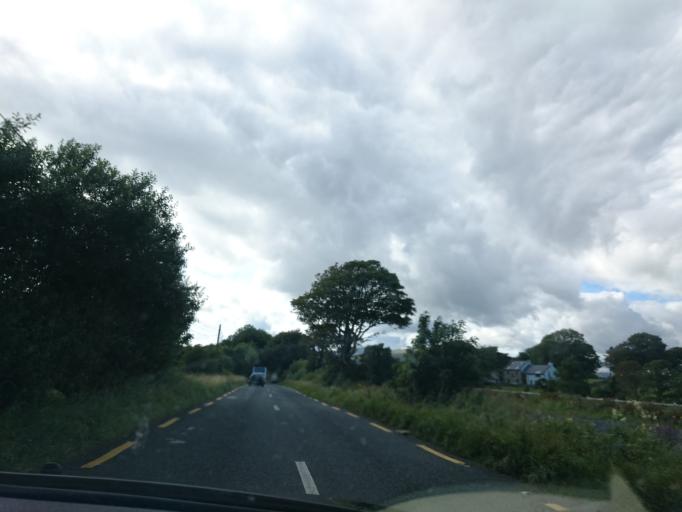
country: IE
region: Connaught
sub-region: Maigh Eo
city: Westport
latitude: 53.9004
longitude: -9.5668
